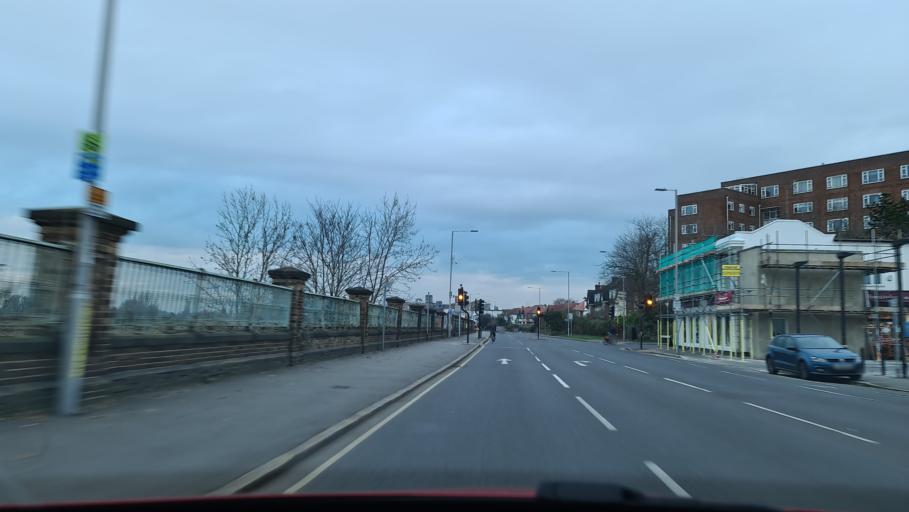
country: GB
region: England
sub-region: Surrey
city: Ditton Hill
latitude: 51.3937
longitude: -0.3150
